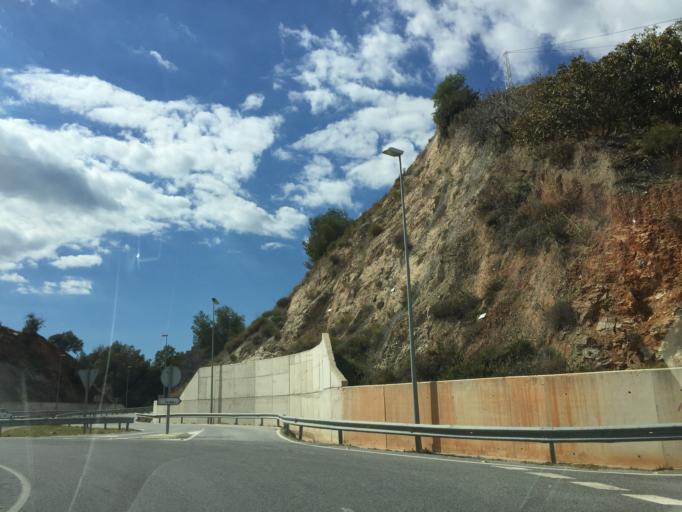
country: ES
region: Andalusia
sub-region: Provincia de Granada
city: La Herradura
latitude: 36.7508
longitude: -3.7830
